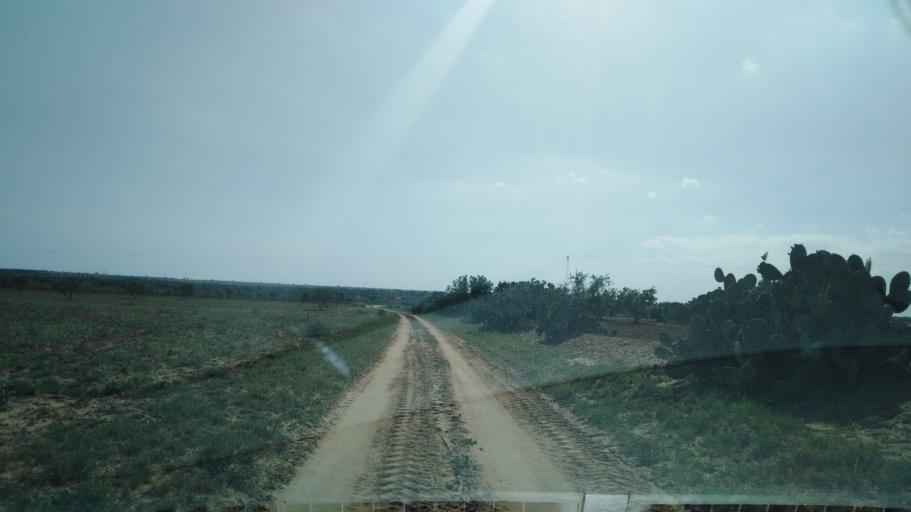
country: TN
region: Safaqis
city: Bi'r `Ali Bin Khalifah
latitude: 34.7817
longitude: 10.3652
